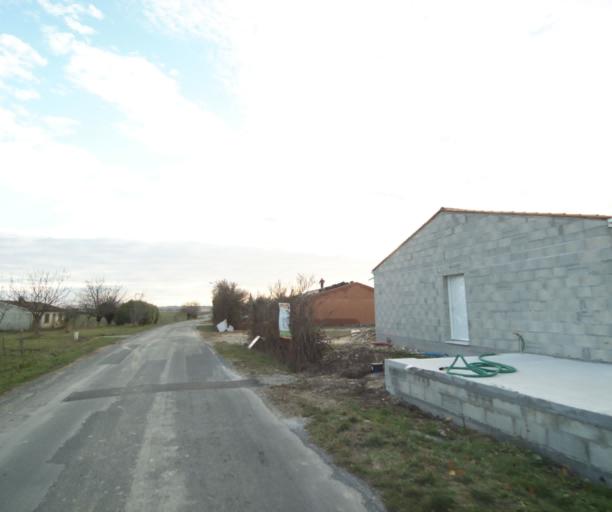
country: FR
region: Poitou-Charentes
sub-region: Departement de la Charente-Maritime
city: Les Gonds
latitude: 45.7053
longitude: -0.5942
